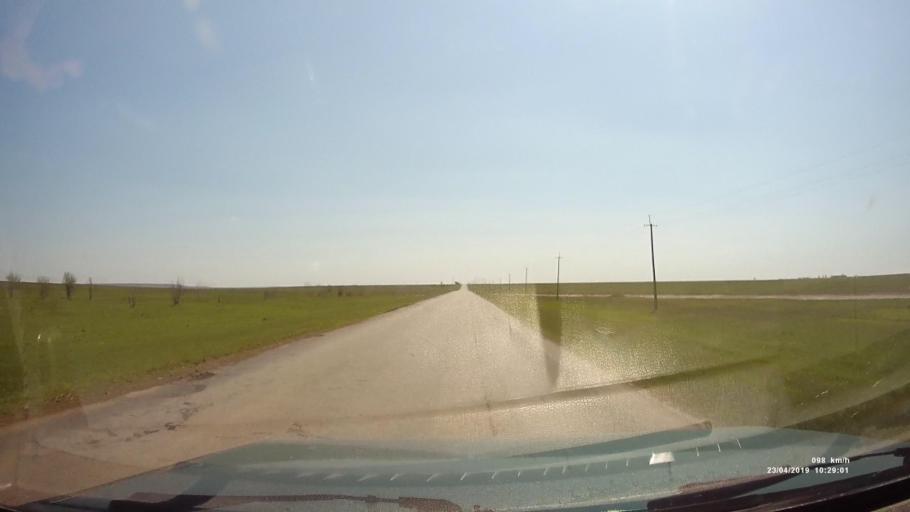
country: RU
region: Kalmykiya
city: Yashalta
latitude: 46.6013
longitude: 42.5186
